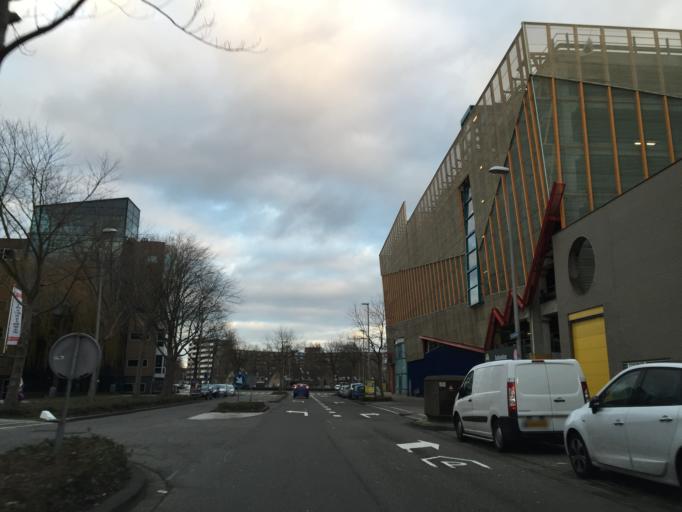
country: NL
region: South Holland
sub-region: Gemeente Zoetermeer
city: Zoetermeer
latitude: 52.0626
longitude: 4.4937
